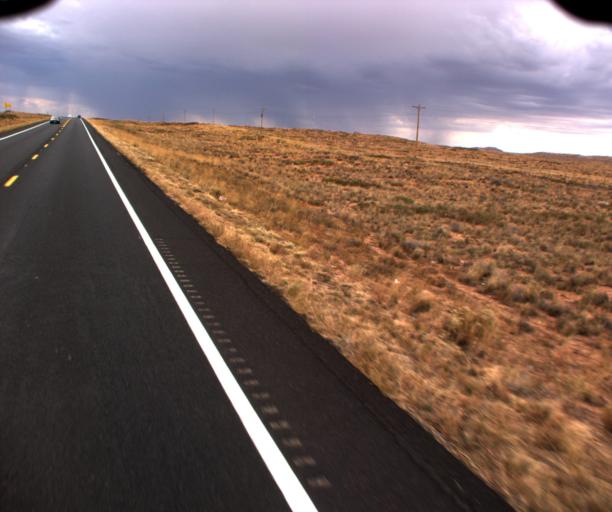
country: US
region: Arizona
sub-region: Coconino County
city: Tuba City
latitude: 36.2985
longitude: -110.9799
